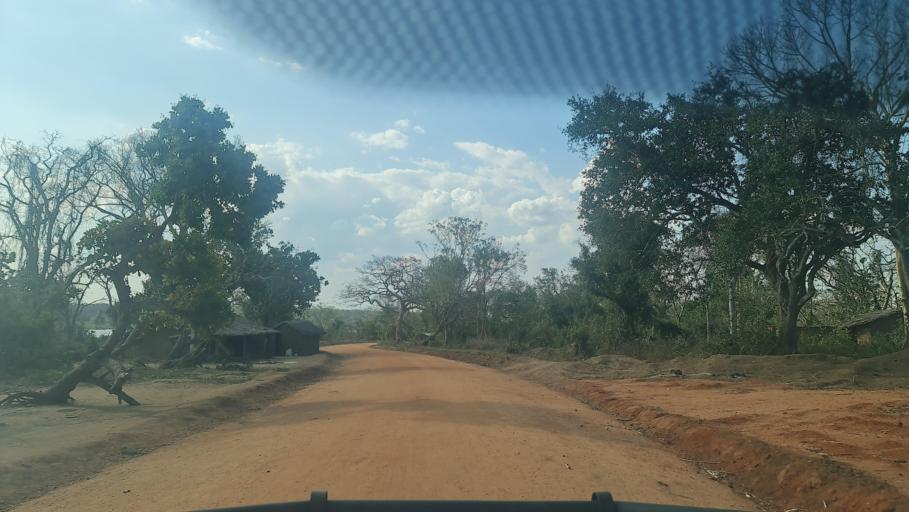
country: MZ
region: Nampula
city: Ilha de Mocambique
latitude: -15.5002
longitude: 40.1604
